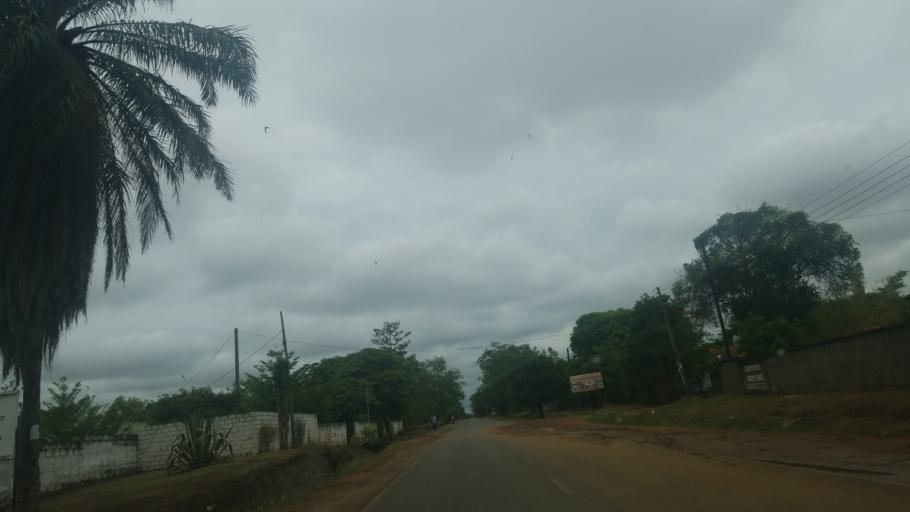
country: ZM
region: Luapula
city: Mansa
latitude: -11.1977
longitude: 28.8938
